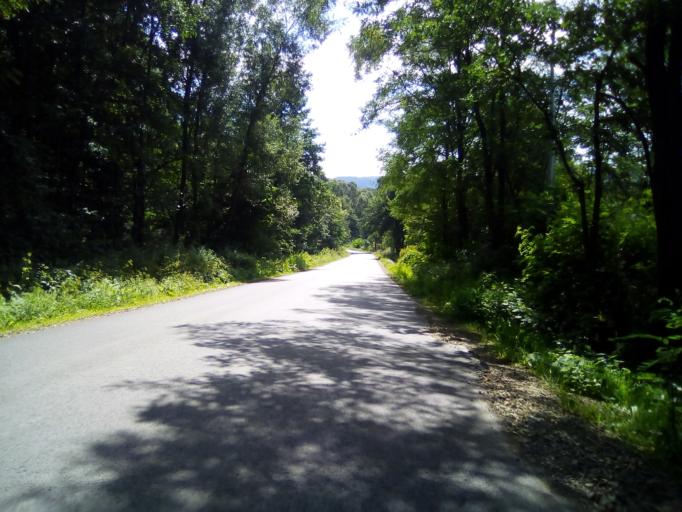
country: PL
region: Subcarpathian Voivodeship
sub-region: Powiat strzyzowski
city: Konieczkowa
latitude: 49.8195
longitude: 21.9255
